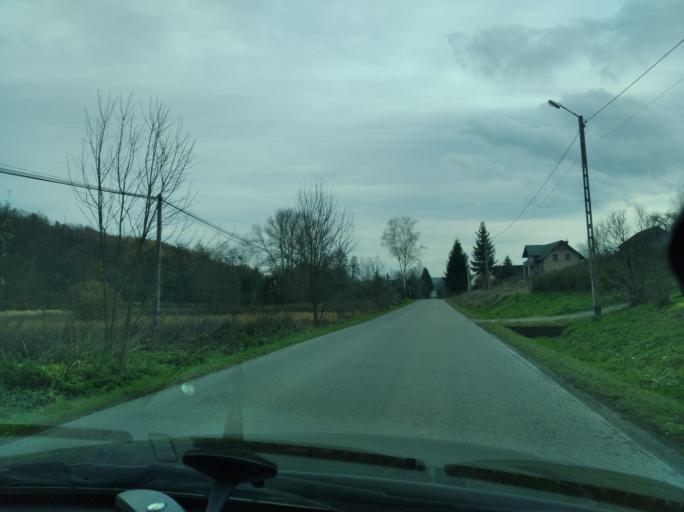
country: PL
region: Subcarpathian Voivodeship
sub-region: Powiat strzyzowski
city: Strzyzow
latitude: 49.9411
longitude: 21.7539
